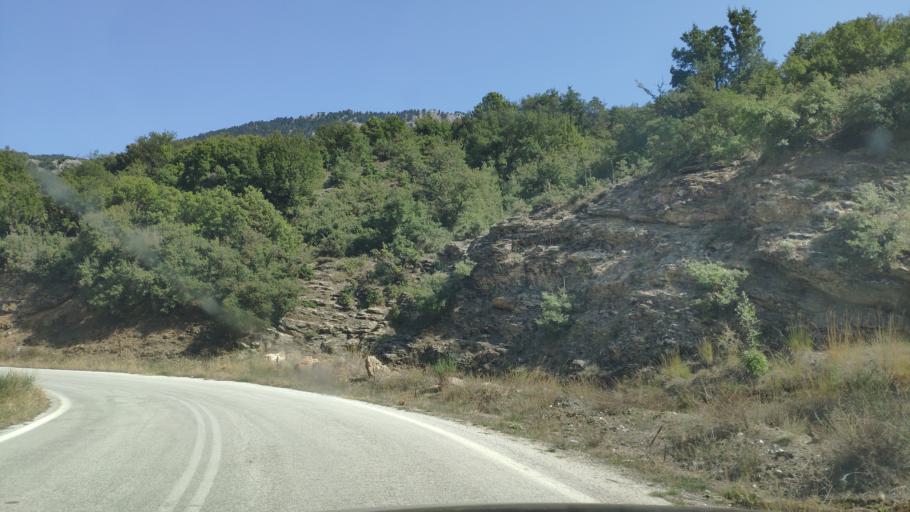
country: GR
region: West Greece
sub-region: Nomos Achaias
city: Aiyira
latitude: 37.9188
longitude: 22.3374
